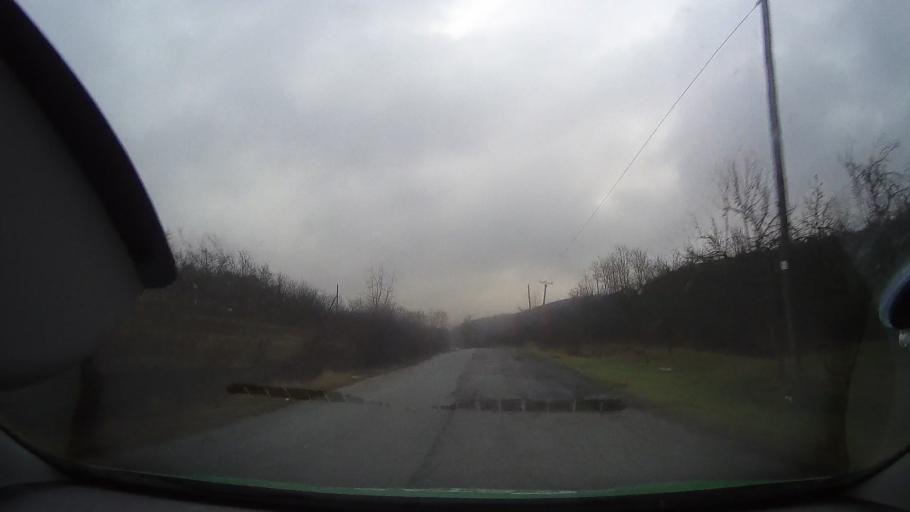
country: RO
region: Hunedoara
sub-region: Comuna Ribita
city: Ribita
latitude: 46.2317
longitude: 22.7417
